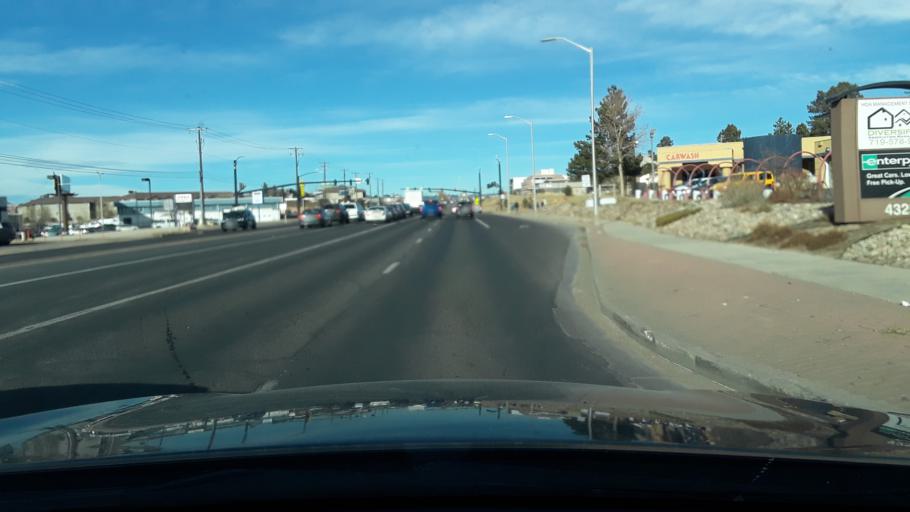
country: US
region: Colorado
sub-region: El Paso County
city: Colorado Springs
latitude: 38.8961
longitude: -104.8182
